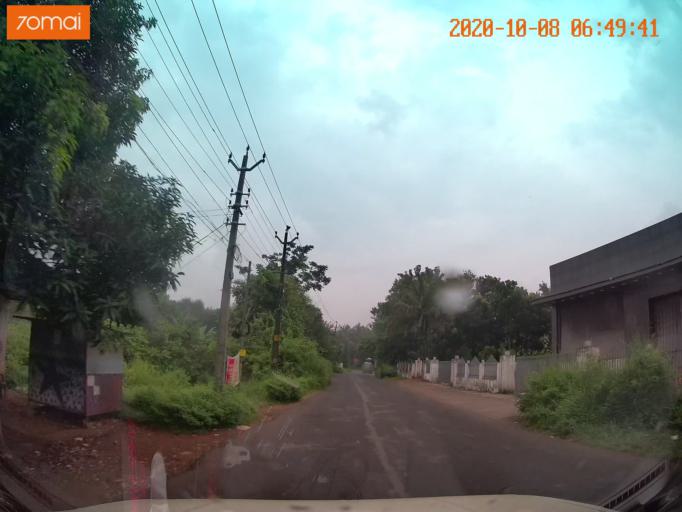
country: IN
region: Kerala
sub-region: Thrissur District
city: Kunnamkulam
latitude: 10.6853
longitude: 76.1027
